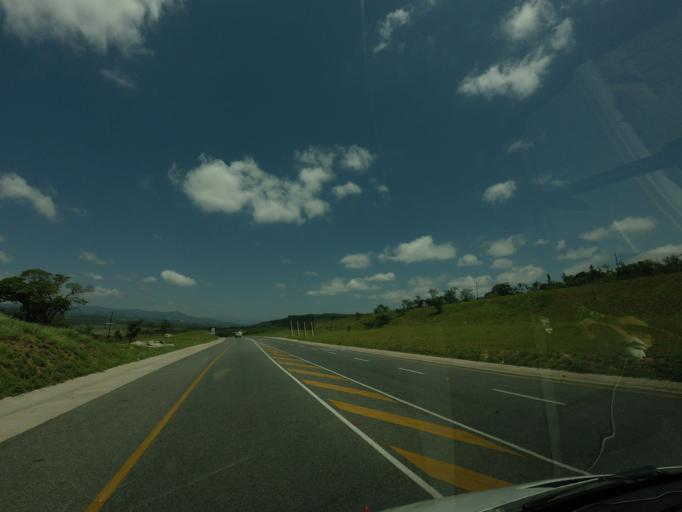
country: ZA
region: Mpumalanga
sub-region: Ehlanzeni District
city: Nelspruit
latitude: -25.4383
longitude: 30.9467
